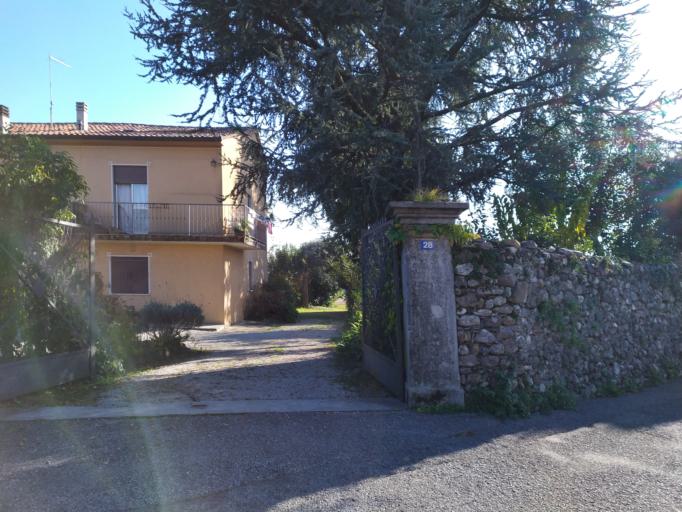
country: IT
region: Veneto
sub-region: Provincia di Vicenza
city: San Vito di Leguzzano
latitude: 45.6975
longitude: 11.3750
